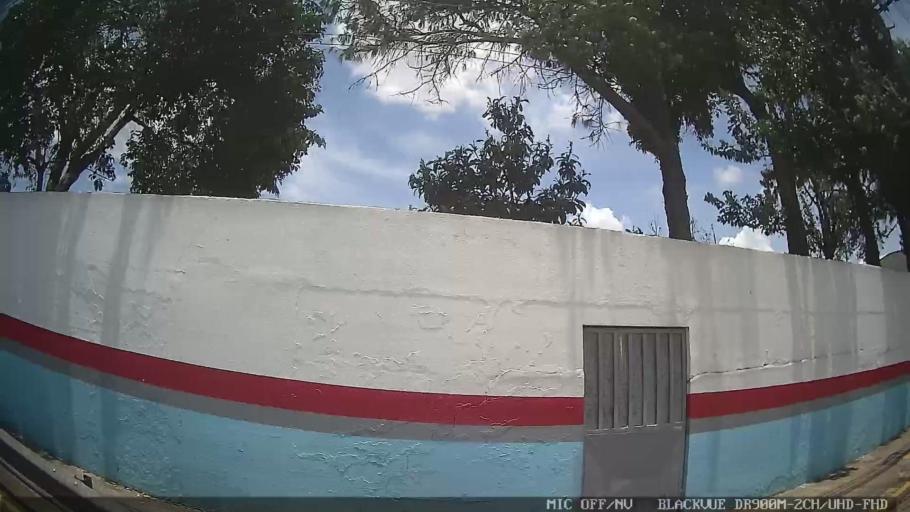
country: BR
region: Sao Paulo
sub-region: Suzano
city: Suzano
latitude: -23.5372
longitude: -46.3037
